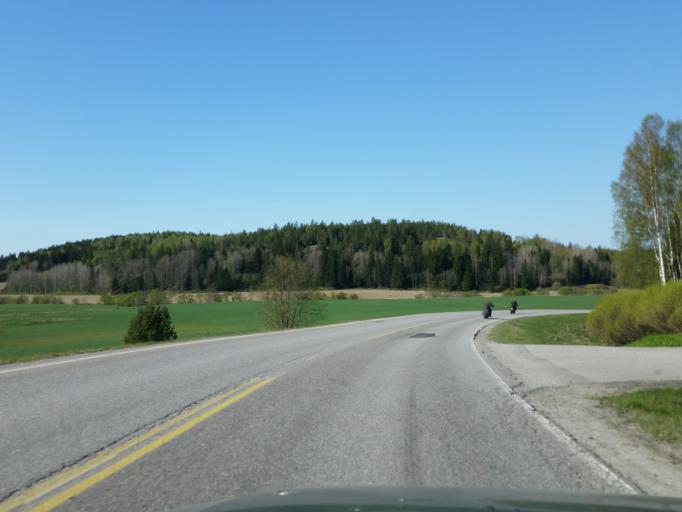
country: FI
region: Uusimaa
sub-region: Helsinki
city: Siuntio
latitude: 60.1785
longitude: 24.2310
